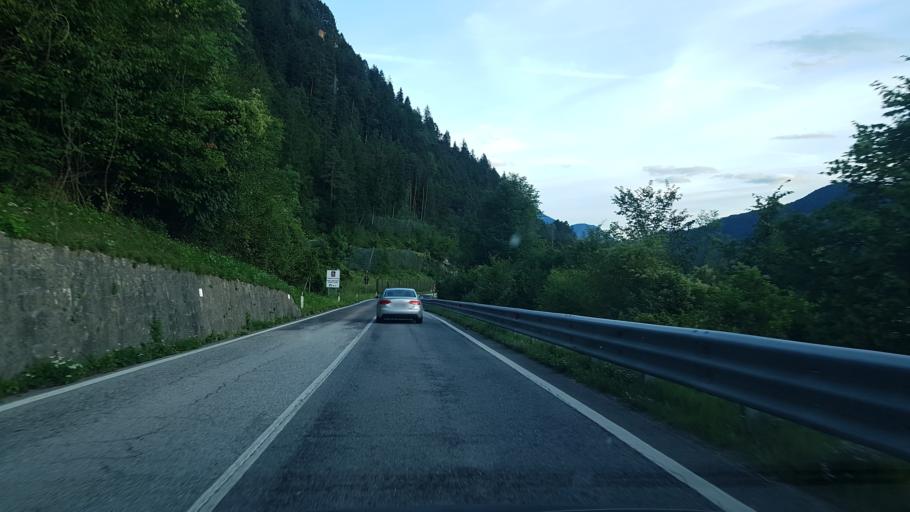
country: IT
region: Friuli Venezia Giulia
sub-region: Provincia di Udine
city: Comeglians
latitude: 46.5049
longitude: 12.8651
